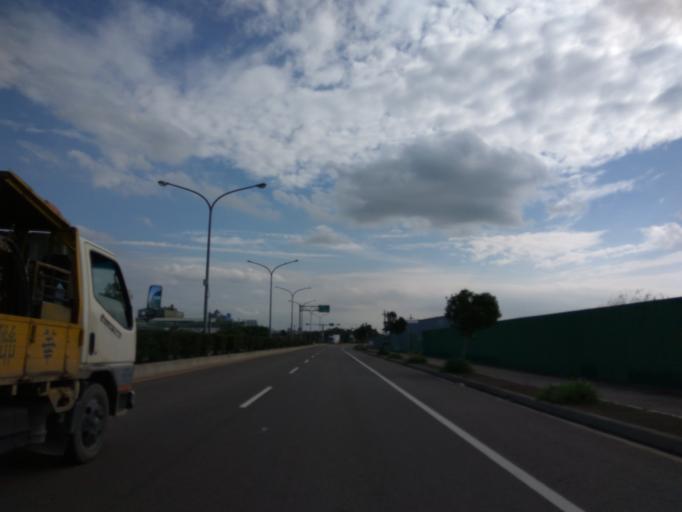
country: TW
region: Taiwan
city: Taoyuan City
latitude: 25.0747
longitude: 121.1717
